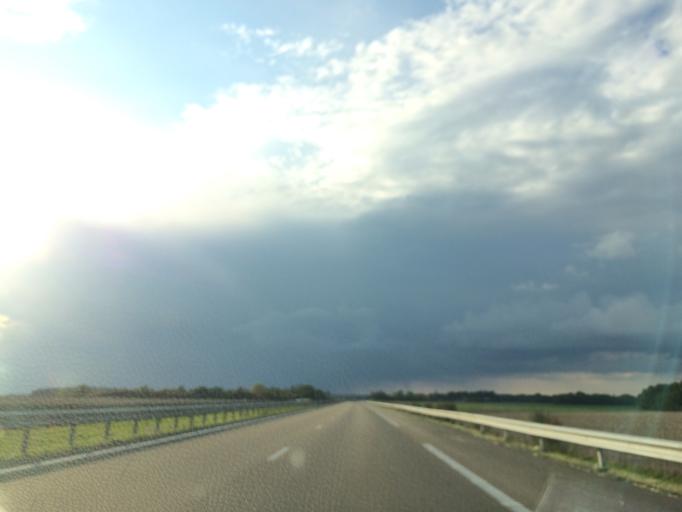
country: FR
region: Ile-de-France
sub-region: Departement de Seine-et-Marne
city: Egreville
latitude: 48.1319
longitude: 2.9464
